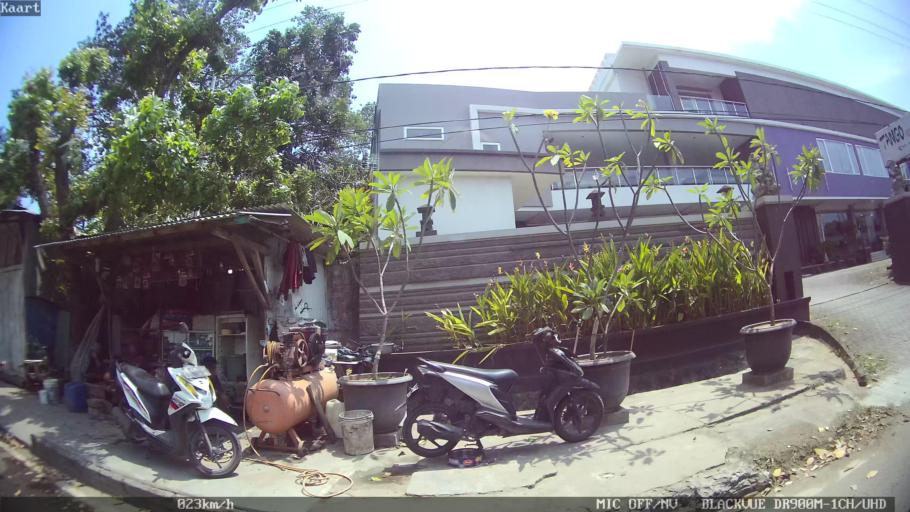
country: ID
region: Lampung
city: Kedaton
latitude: -5.3790
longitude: 105.2633
